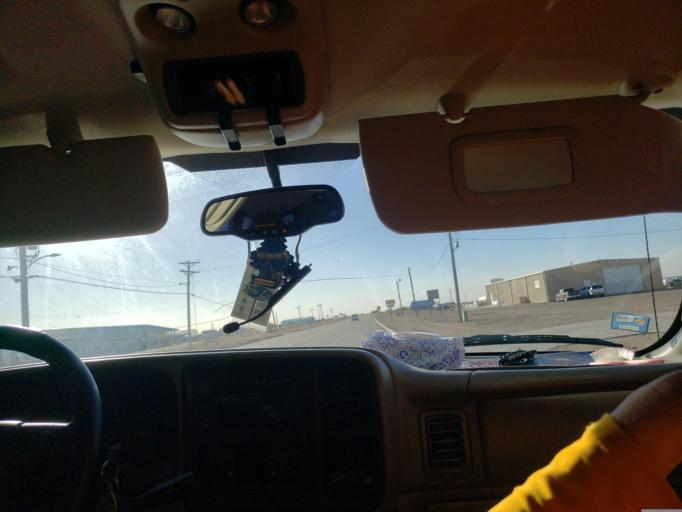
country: US
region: Kansas
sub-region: Haskell County
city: Satanta
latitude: 37.4380
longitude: -100.9950
